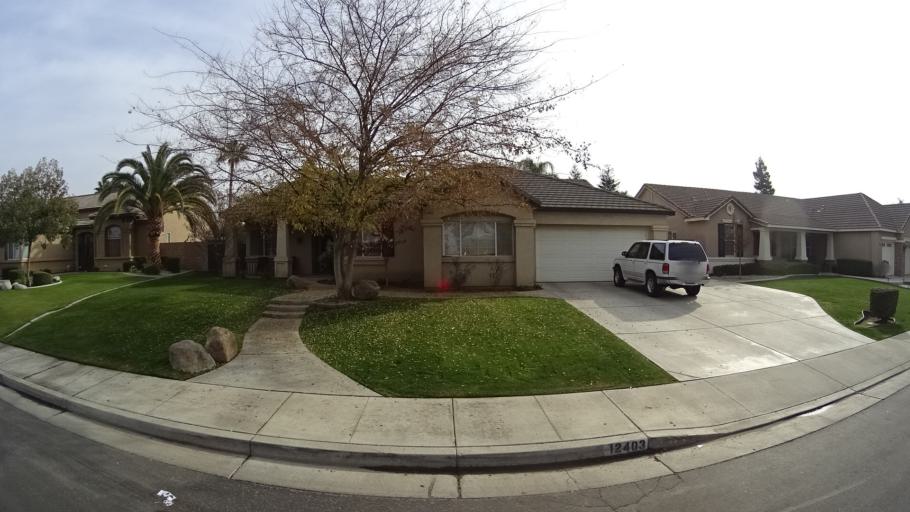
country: US
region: California
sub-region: Kern County
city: Rosedale
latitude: 35.3453
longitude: -119.1406
